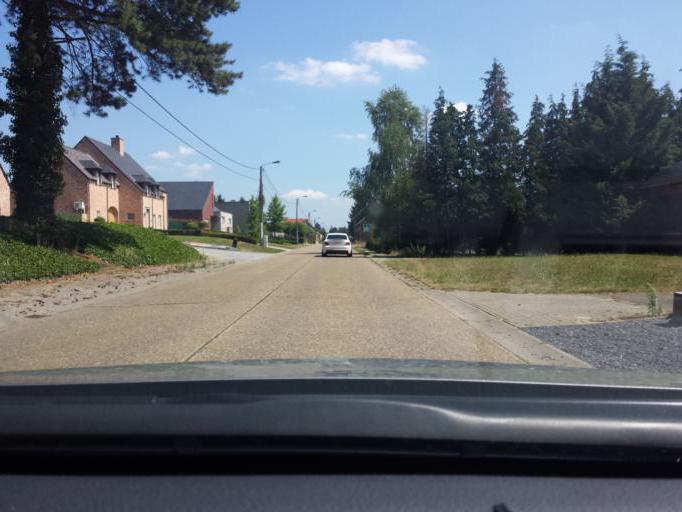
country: BE
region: Flanders
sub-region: Provincie Limburg
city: Halen
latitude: 50.9935
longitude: 5.1297
